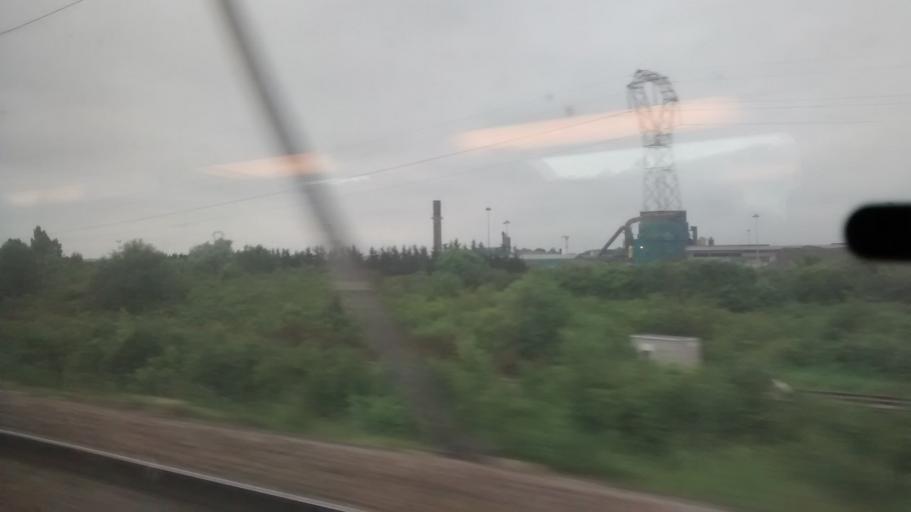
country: FR
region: Ile-de-France
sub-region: Departement de Seine-et-Marne
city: Saint-Germain-Laval
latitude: 48.3916
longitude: 2.9847
